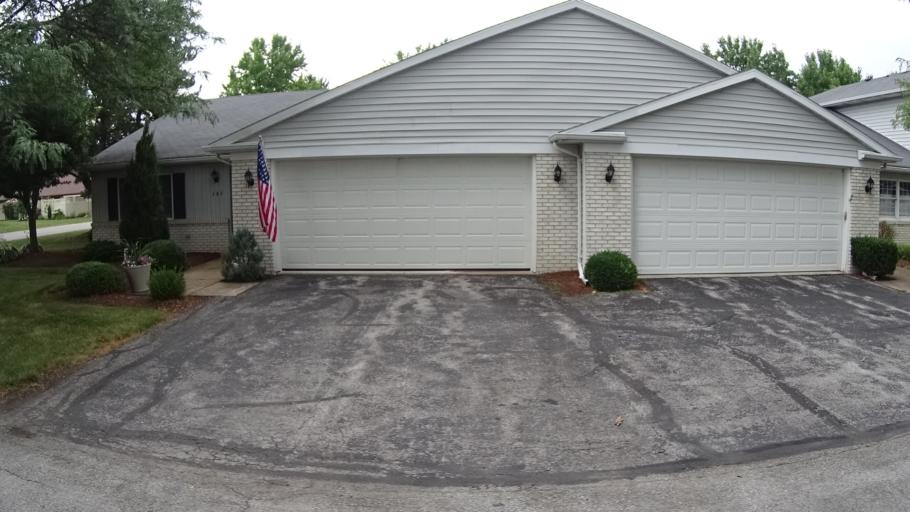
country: US
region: Ohio
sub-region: Erie County
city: Sandusky
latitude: 41.4391
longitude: -82.7689
